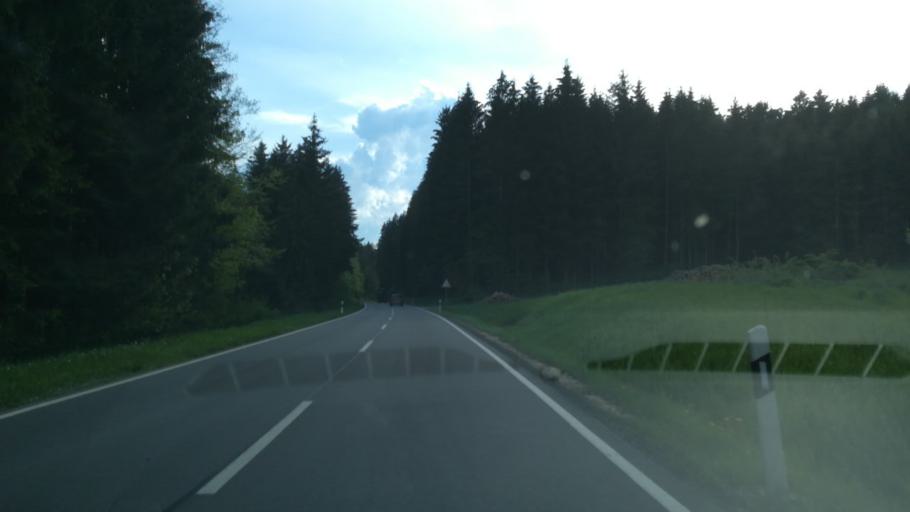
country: DE
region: Baden-Wuerttemberg
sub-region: Freiburg Region
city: Muhlingen
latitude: 47.9049
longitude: 9.0225
